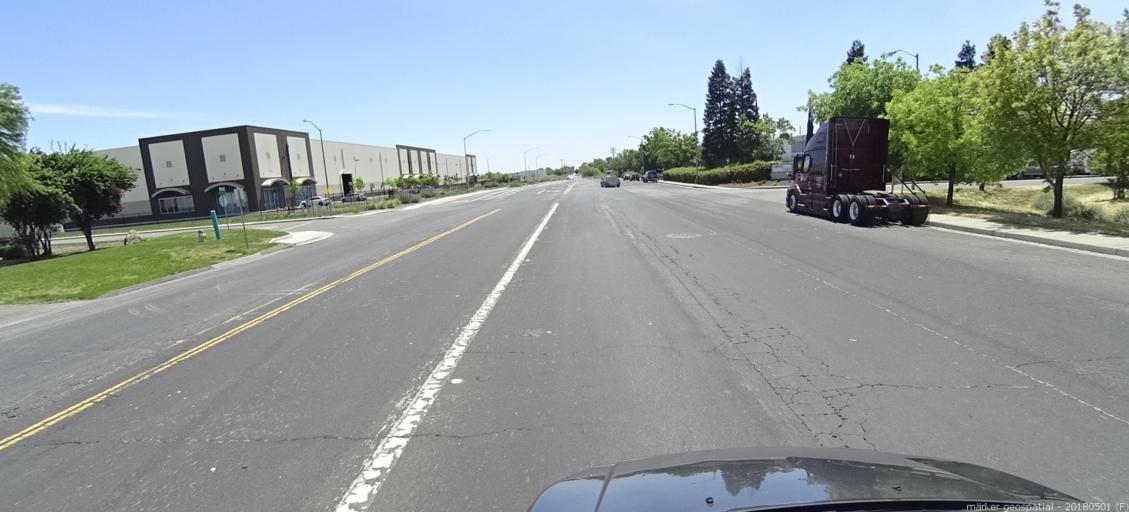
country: US
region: California
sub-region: Sacramento County
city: Rio Linda
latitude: 38.6660
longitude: -121.4292
